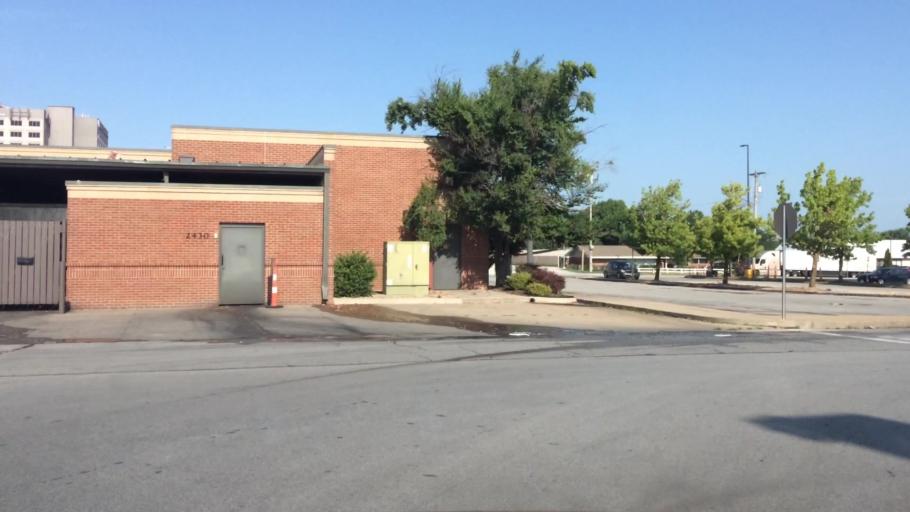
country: US
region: Missouri
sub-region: Greene County
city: Springfield
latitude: 37.2412
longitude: -93.2598
